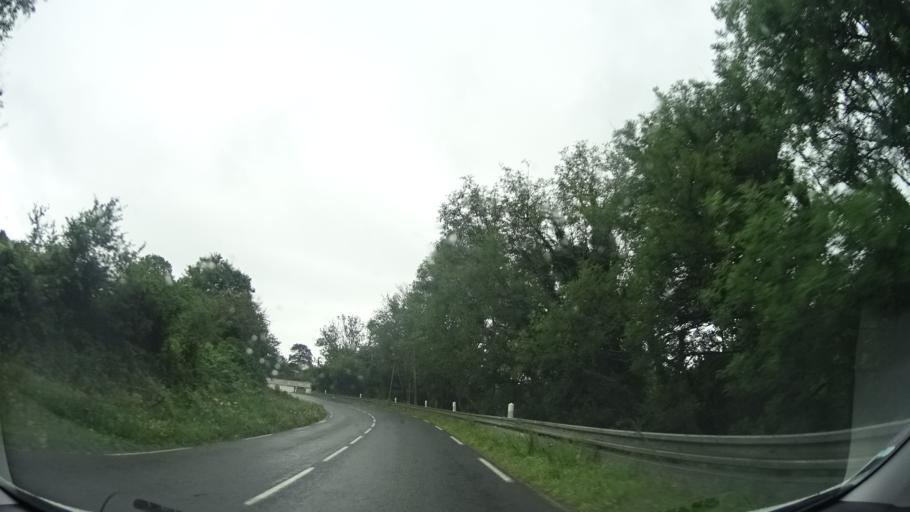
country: FR
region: Lower Normandy
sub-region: Departement de la Manche
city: Beaumont-Hague
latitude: 49.6094
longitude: -1.7911
